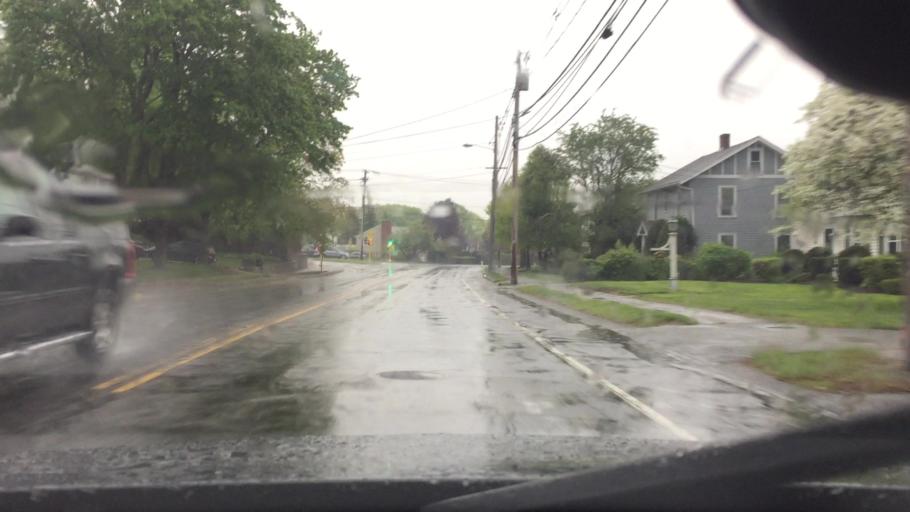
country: US
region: Massachusetts
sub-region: Norfolk County
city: Needham
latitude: 42.2716
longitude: -71.2068
